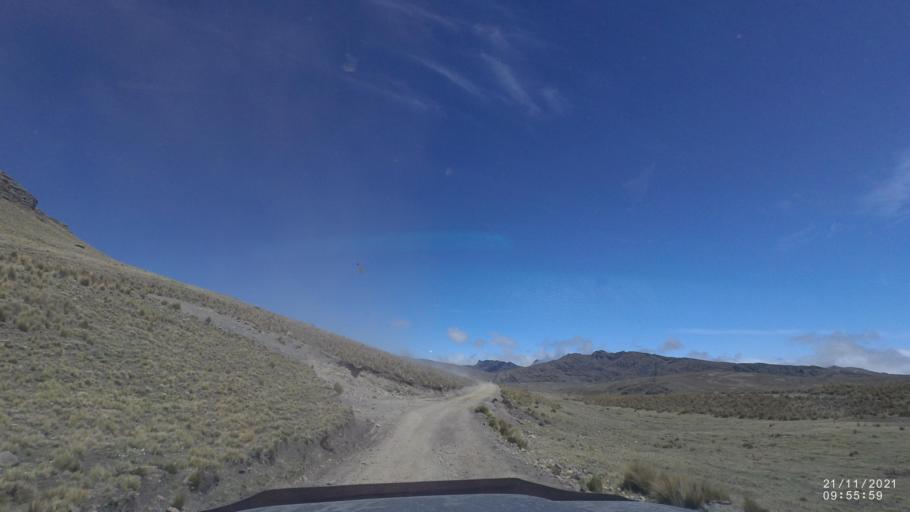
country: BO
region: Cochabamba
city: Cochabamba
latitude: -17.0439
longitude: -66.2647
